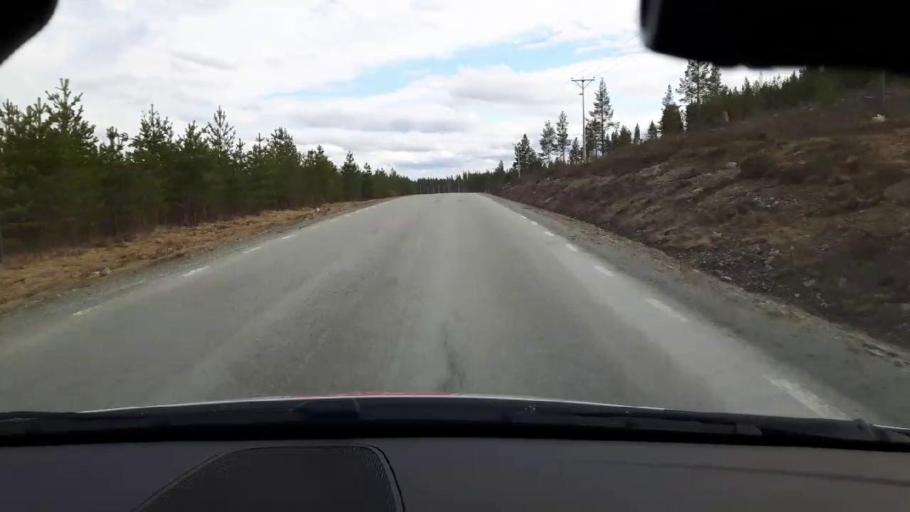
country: SE
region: Jaemtland
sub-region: Bergs Kommun
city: Hoverberg
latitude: 62.7114
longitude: 14.6106
